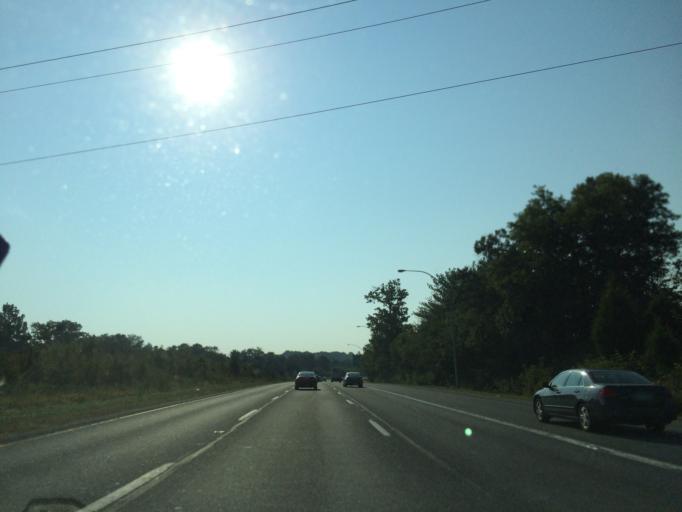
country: US
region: Maryland
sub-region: Howard County
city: Riverside
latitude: 39.1715
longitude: -76.8474
